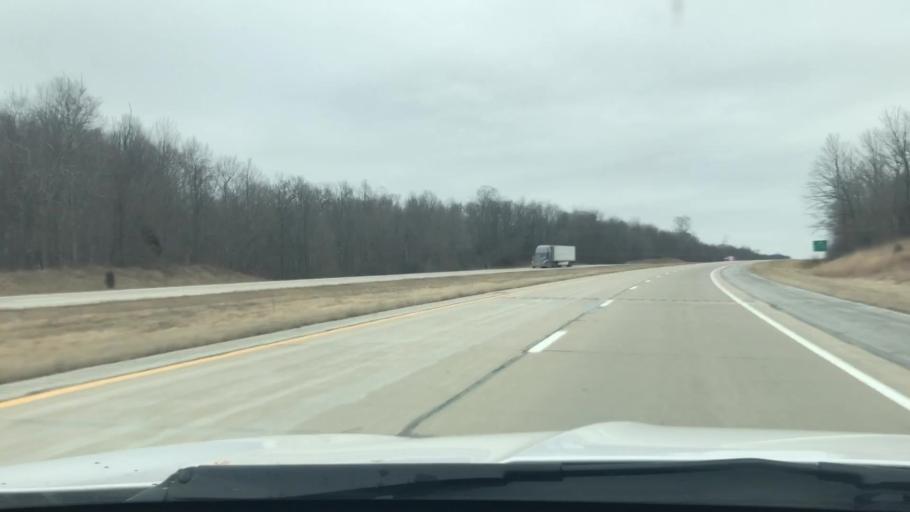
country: US
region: Indiana
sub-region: Miami County
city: Peru
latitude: 40.7691
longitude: -86.1615
